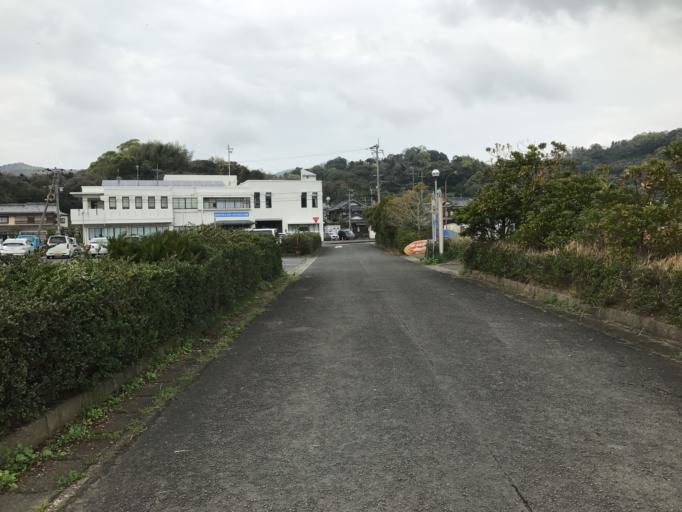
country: JP
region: Nagasaki
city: Nagasaki-shi
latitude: 32.7076
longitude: 129.9132
